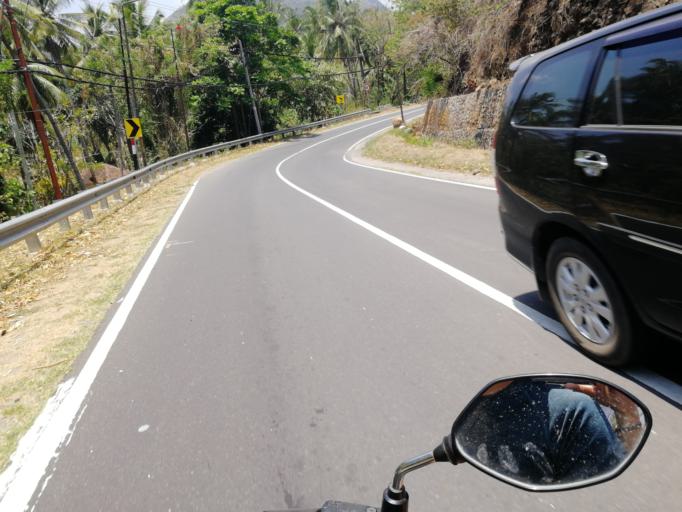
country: ID
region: West Nusa Tenggara
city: Karangsubagan
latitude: -8.4436
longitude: 116.0370
